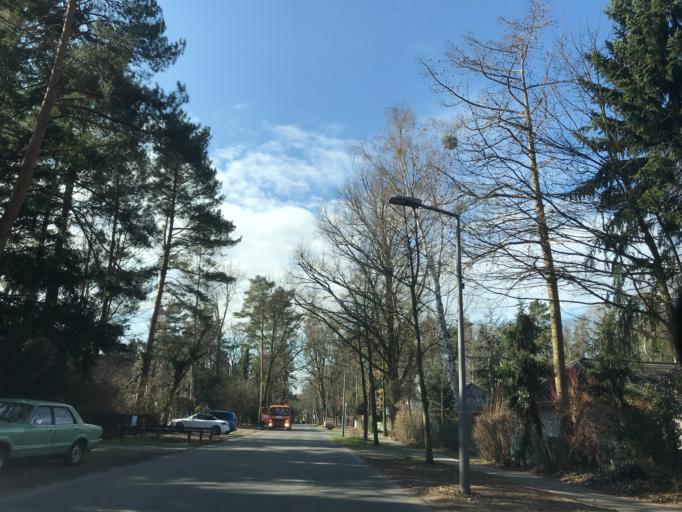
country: DE
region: Berlin
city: Kladow
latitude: 52.4584
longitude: 13.1249
